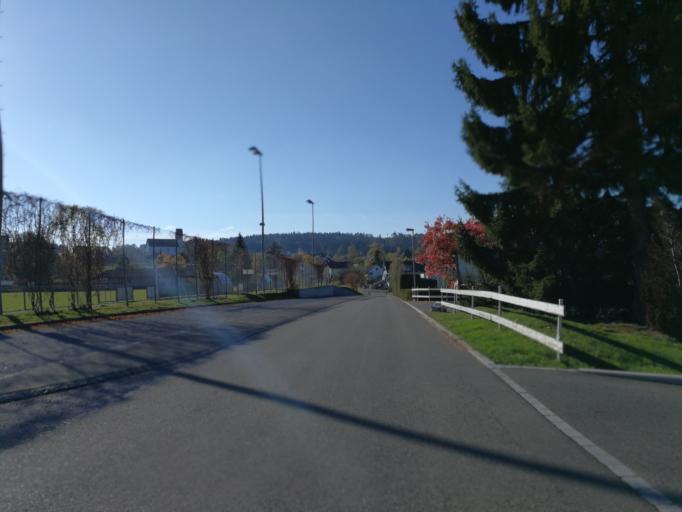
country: CH
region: Zurich
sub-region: Bezirk Meilen
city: Oetwil am See
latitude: 47.2725
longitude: 8.7293
